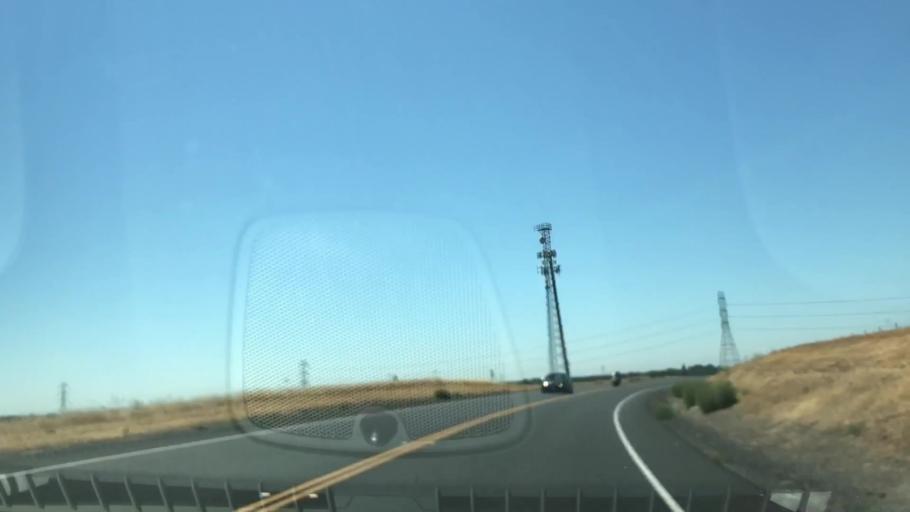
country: US
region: California
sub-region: San Joaquin County
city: Escalon
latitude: 37.9325
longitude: -120.9454
